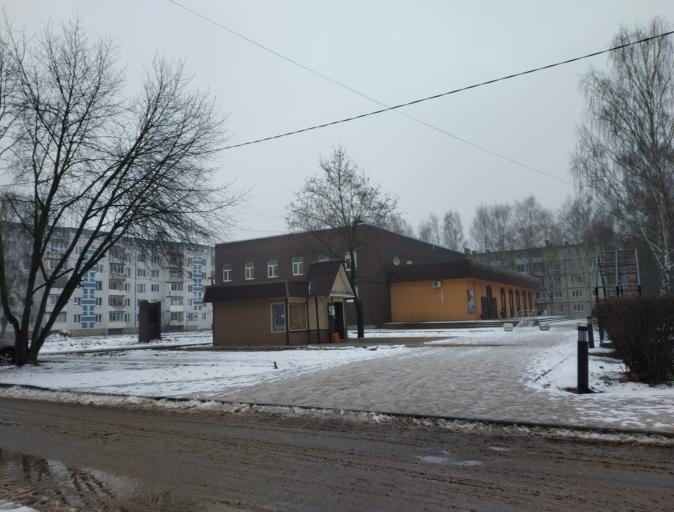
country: RU
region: Moskovskaya
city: Taldom
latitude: 56.7391
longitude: 37.5360
